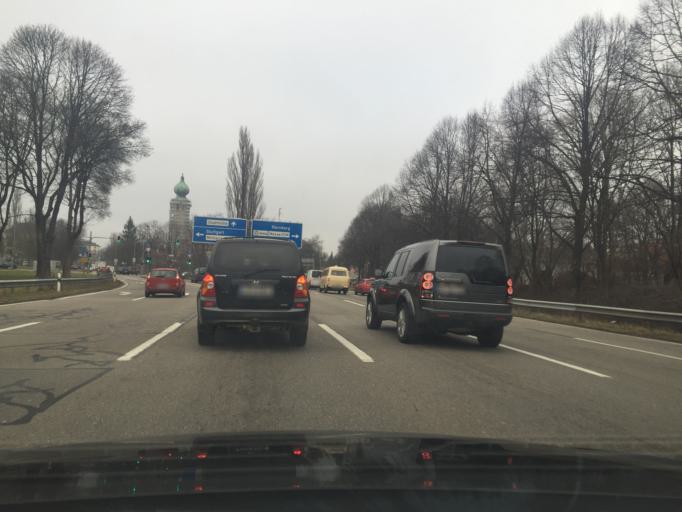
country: DE
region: Bavaria
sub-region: Upper Bavaria
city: Bogenhausen
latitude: 48.1111
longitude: 11.6155
